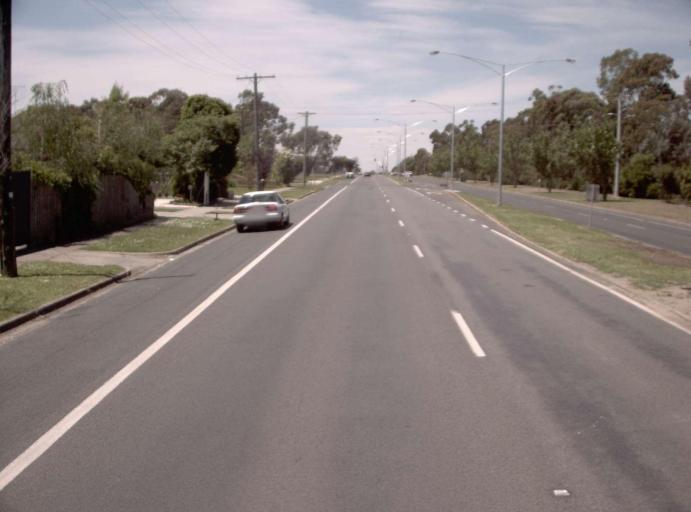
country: AU
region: Victoria
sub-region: Latrobe
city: Traralgon
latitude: -38.2033
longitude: 146.5183
